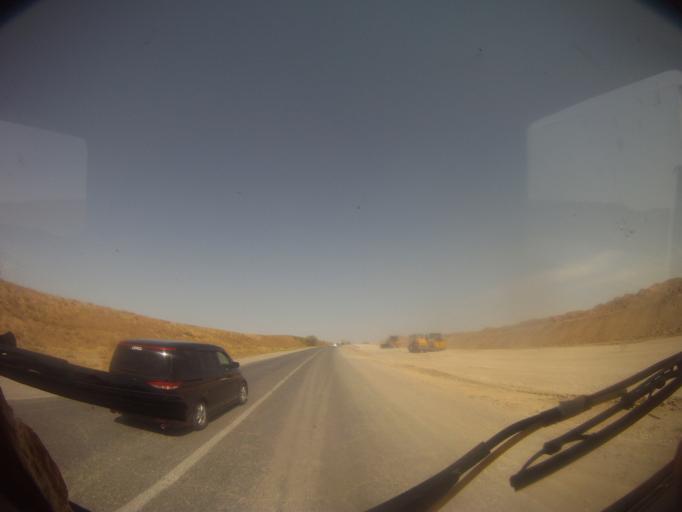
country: KZ
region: Ongtustik Qazaqstan
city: Aksu
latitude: 42.4638
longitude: 69.7700
